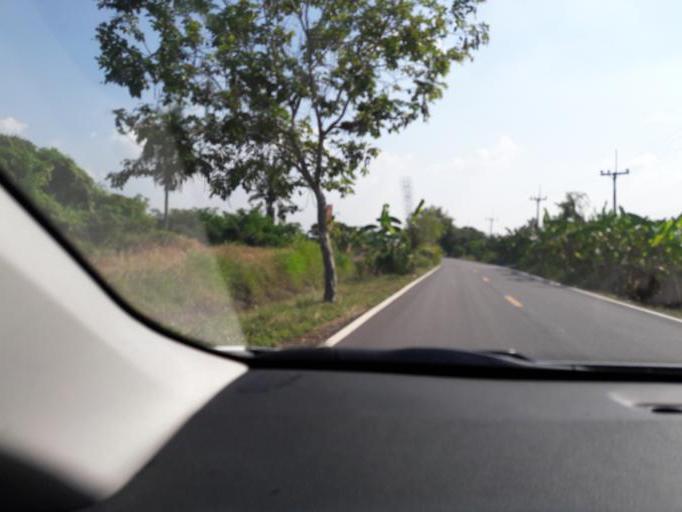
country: TH
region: Ang Thong
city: Wiset Chaichan
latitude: 14.5673
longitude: 100.3887
